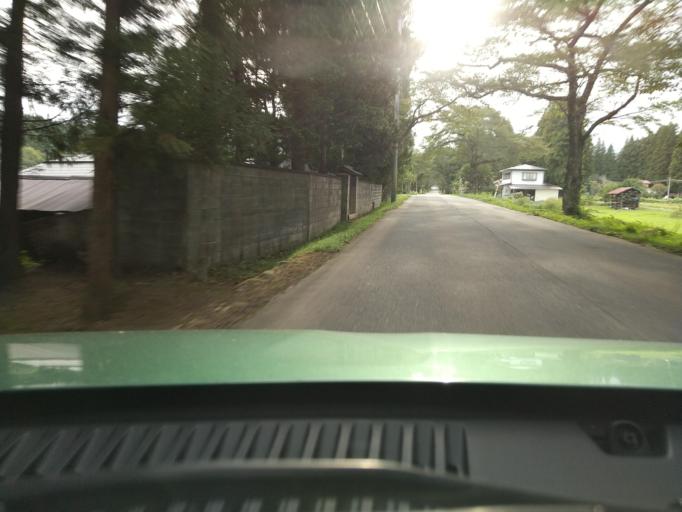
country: JP
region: Iwate
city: Mizusawa
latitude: 39.1228
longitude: 140.9721
